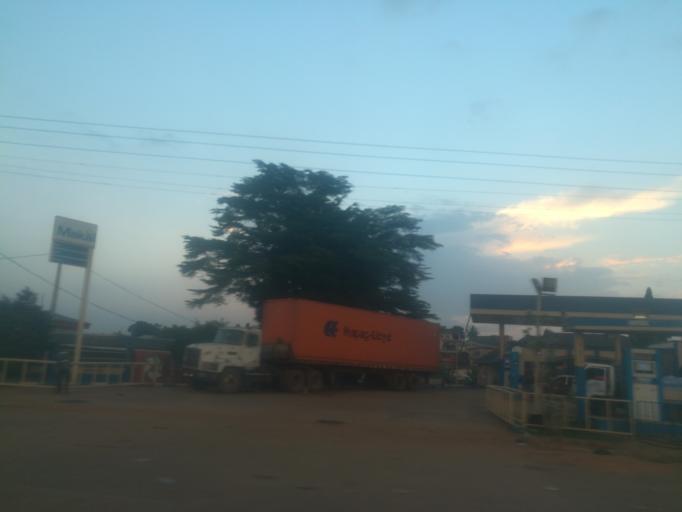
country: NG
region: Oyo
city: Ibadan
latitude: 7.4168
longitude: 3.9418
